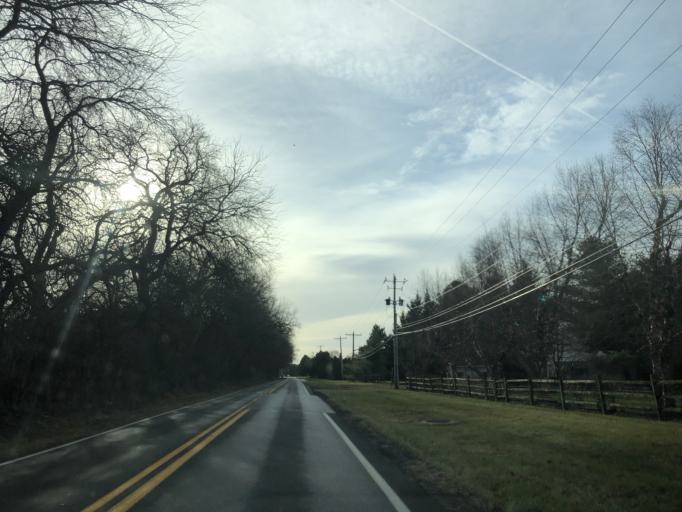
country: US
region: Delaware
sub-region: New Castle County
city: Townsend
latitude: 39.4455
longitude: -75.6463
